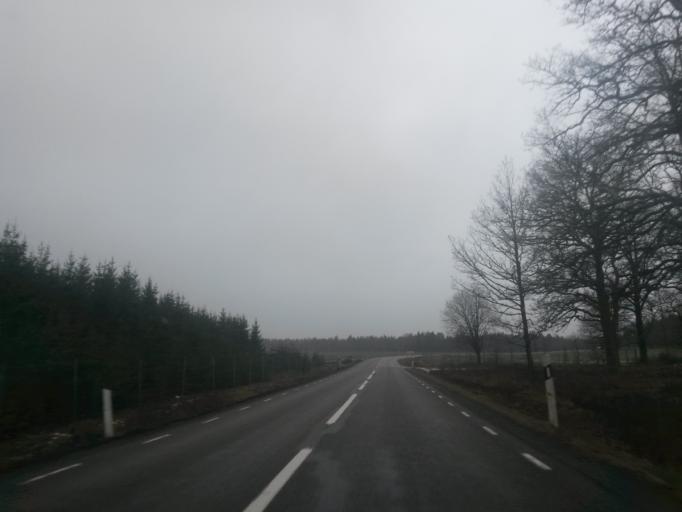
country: SE
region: Vaestra Goetaland
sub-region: Alingsas Kommun
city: Sollebrunn
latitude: 58.1464
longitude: 12.4183
